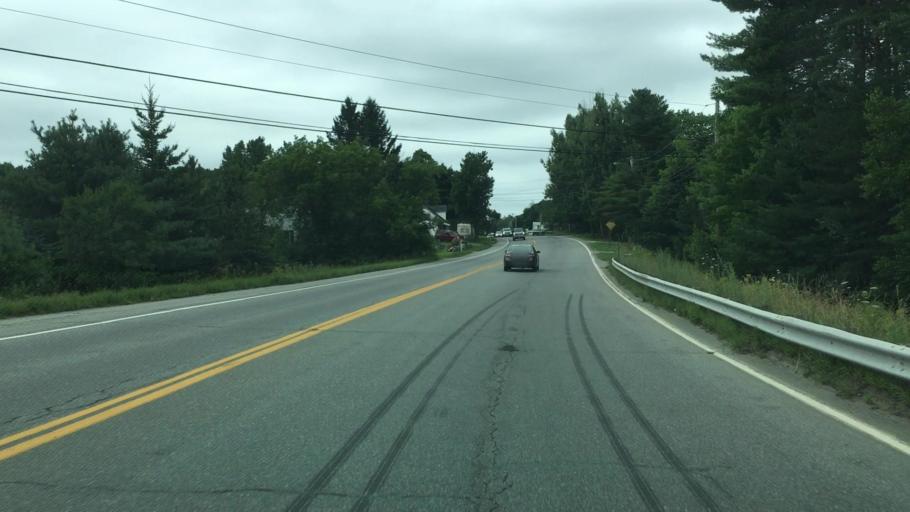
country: US
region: Maine
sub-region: Penobscot County
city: Orrington
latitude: 44.7123
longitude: -68.8471
